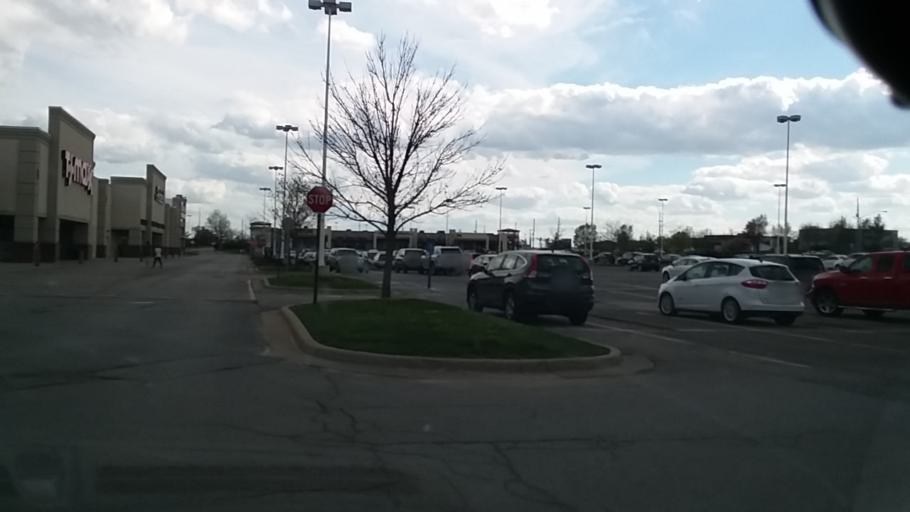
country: US
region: Kansas
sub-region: Douglas County
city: Lawrence
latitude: 38.9277
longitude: -95.2590
